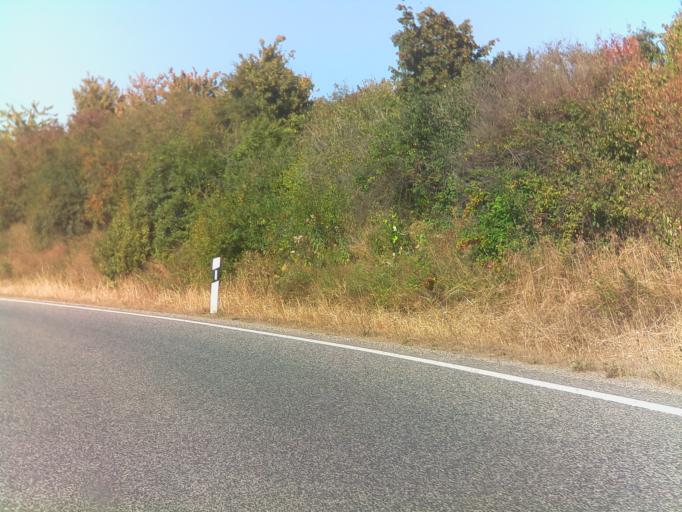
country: DE
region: Hesse
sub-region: Regierungsbezirk Darmstadt
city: Hattersheim
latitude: 50.0683
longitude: 8.4702
